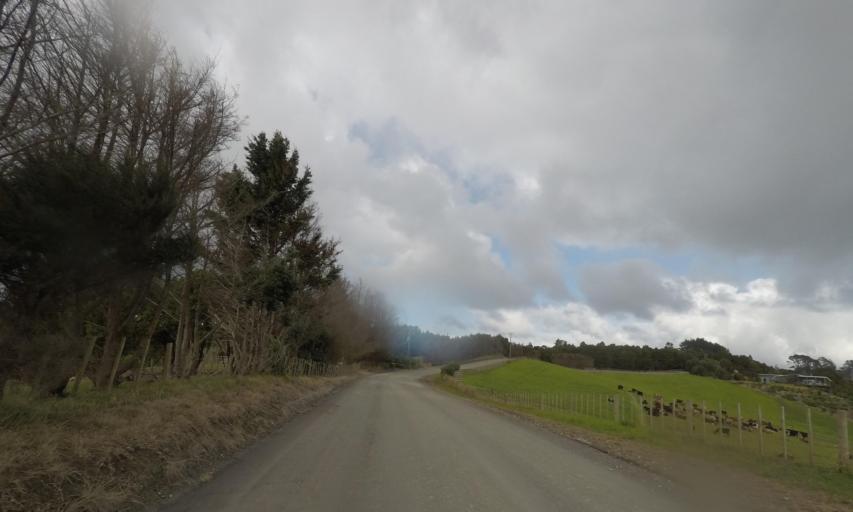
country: NZ
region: Auckland
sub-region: Auckland
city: Wellsford
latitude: -36.1668
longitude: 174.6026
